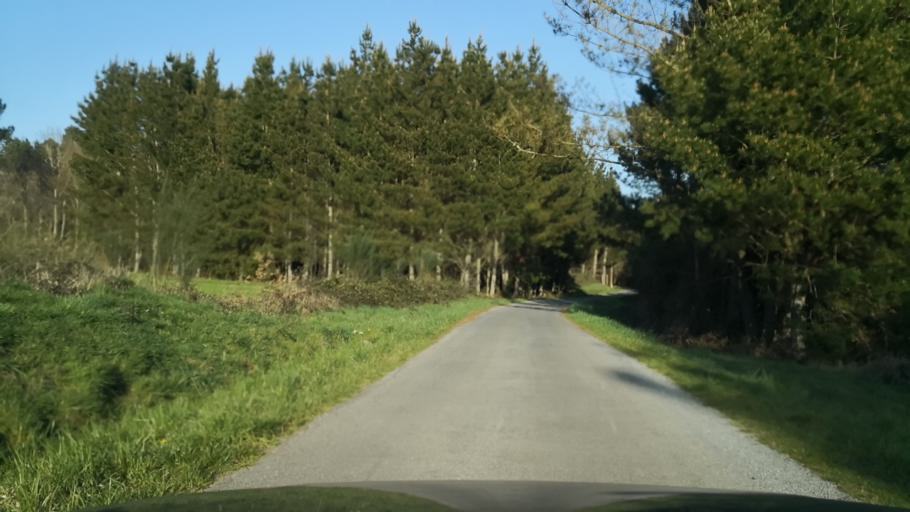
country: ES
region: Galicia
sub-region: Provincia de Lugo
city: Corgo
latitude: 42.9340
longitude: -7.4509
